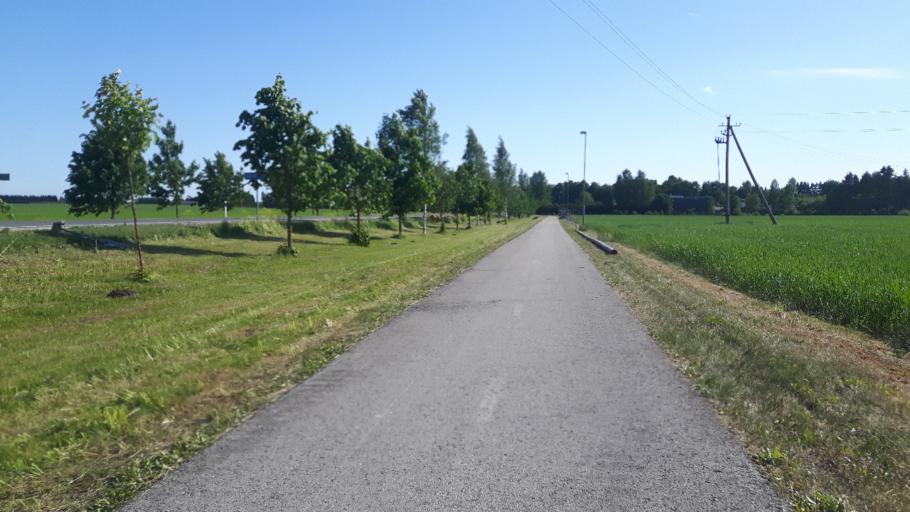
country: EE
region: Raplamaa
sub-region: Kehtna vald
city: Kehtna
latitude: 58.9319
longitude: 24.8793
